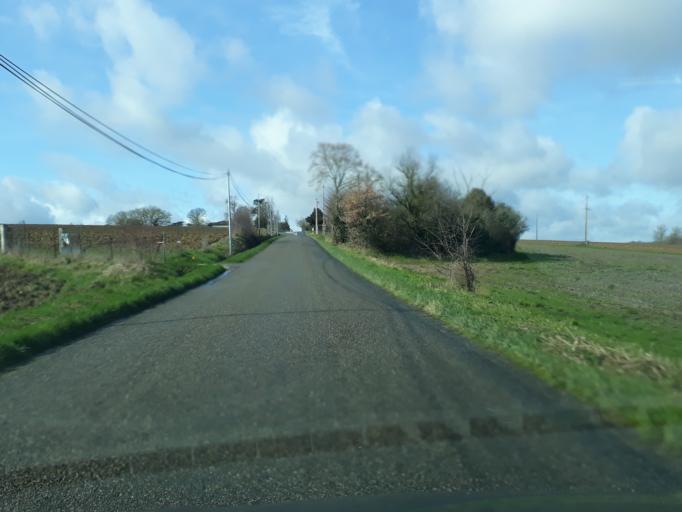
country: FR
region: Midi-Pyrenees
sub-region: Departement du Gers
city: Pujaudran
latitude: 43.6197
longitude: 1.0366
